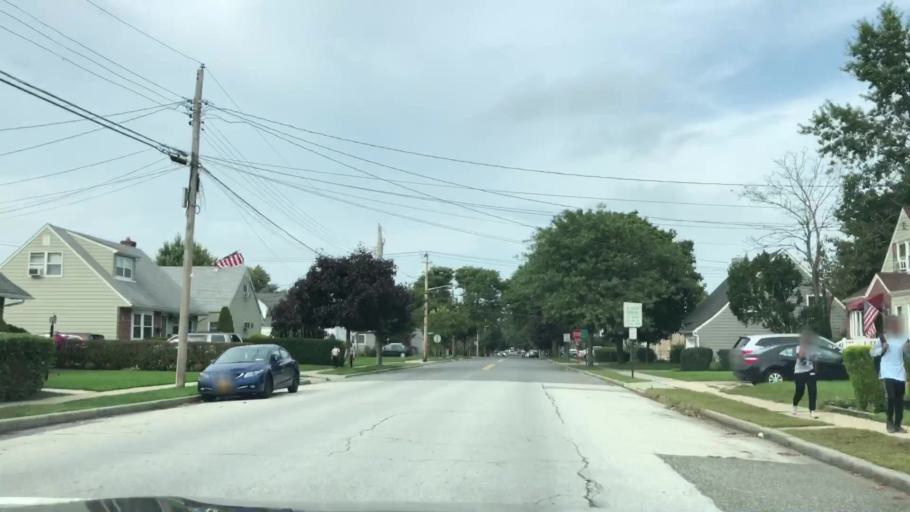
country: US
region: New York
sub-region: Nassau County
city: South Floral Park
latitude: 40.7127
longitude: -73.6931
